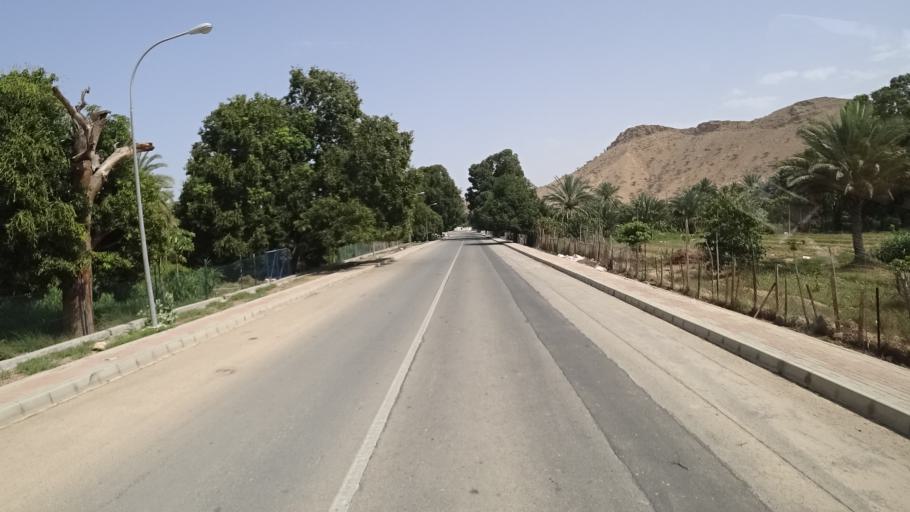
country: OM
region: Muhafazat Masqat
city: Muscat
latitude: 23.1694
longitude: 58.9182
